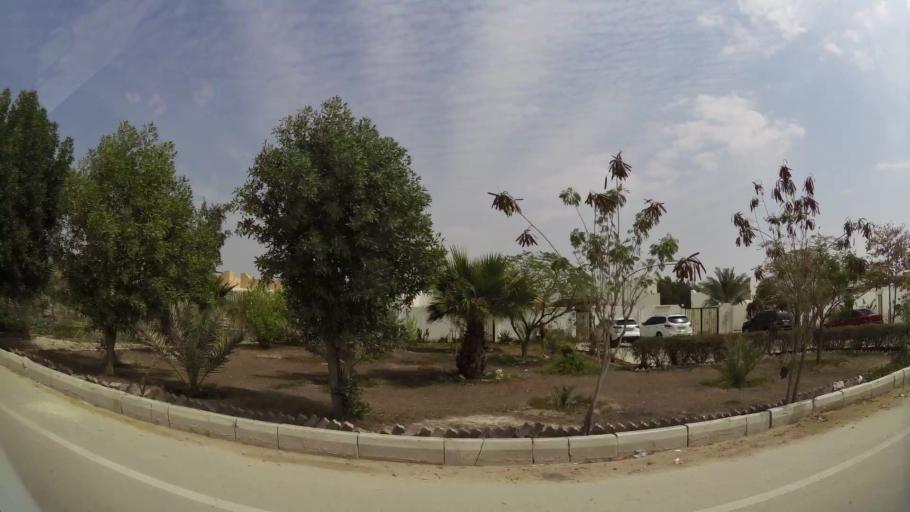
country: AE
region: Abu Dhabi
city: Abu Dhabi
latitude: 24.5288
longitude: 54.6809
